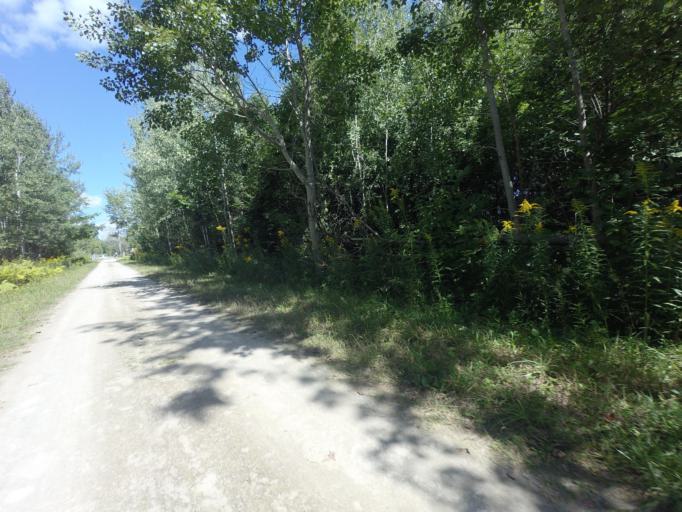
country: CA
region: Ontario
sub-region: Wellington County
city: Guelph
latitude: 43.7600
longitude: -80.3239
